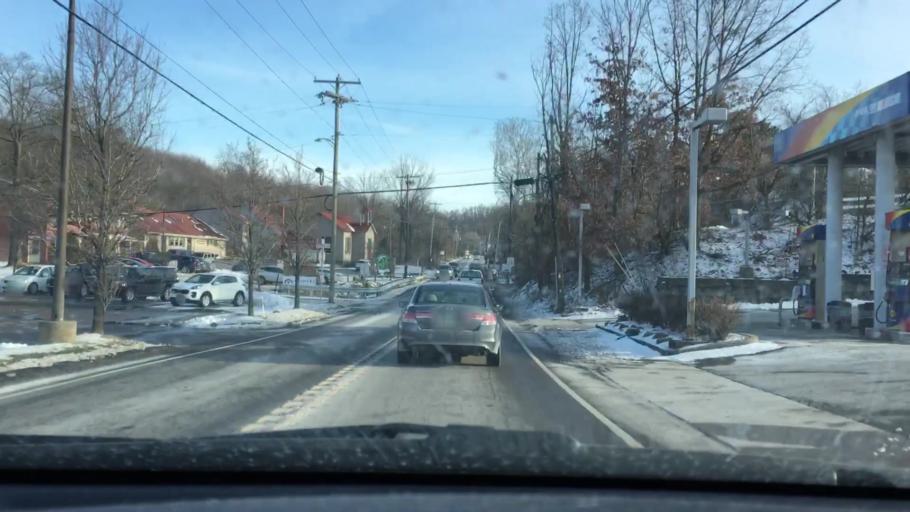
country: US
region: Pennsylvania
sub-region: Washington County
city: Thompsonville
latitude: 40.2724
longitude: -80.1255
